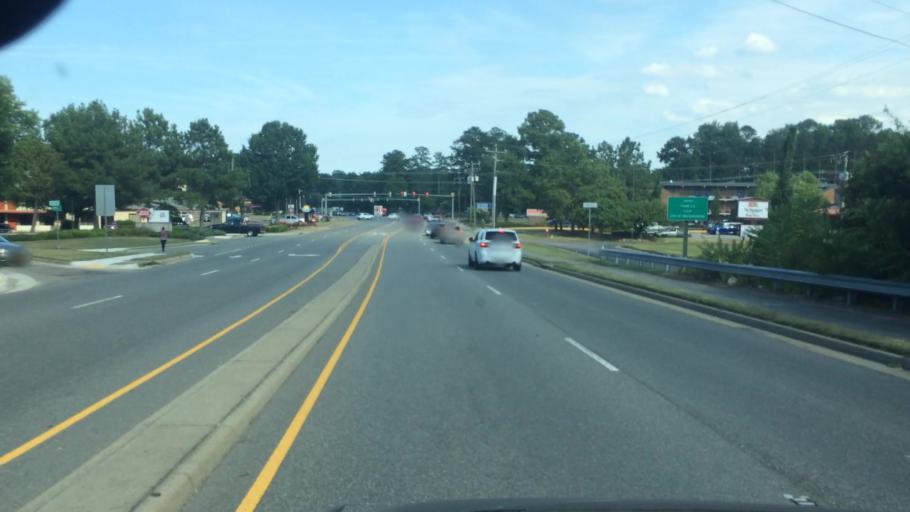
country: US
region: Virginia
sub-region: City of Williamsburg
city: Williamsburg
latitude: 37.2860
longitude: -76.7193
